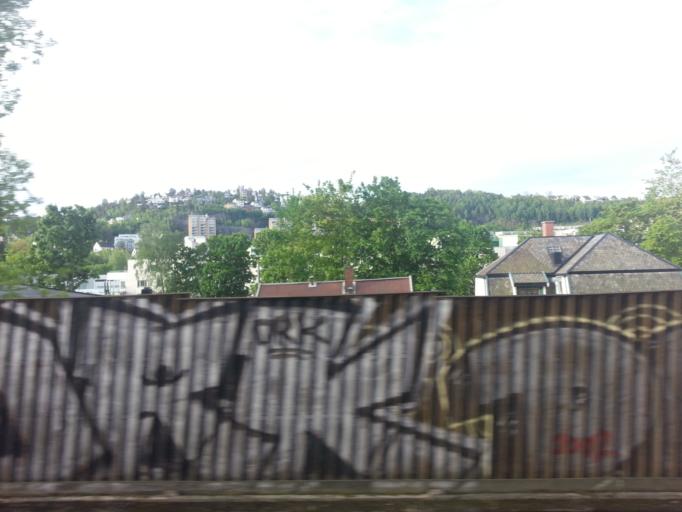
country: NO
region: Oslo
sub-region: Oslo
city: Oslo
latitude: 59.9059
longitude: 10.7890
